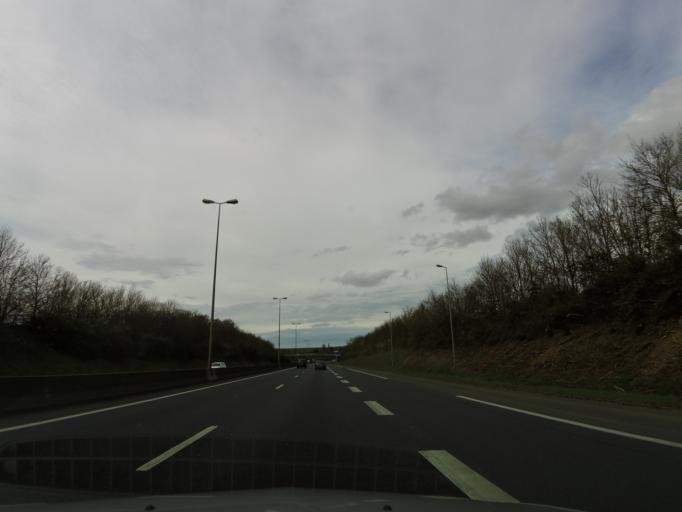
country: FR
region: Lower Normandy
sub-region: Departement du Calvados
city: Eterville
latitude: 49.1550
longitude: -0.4214
